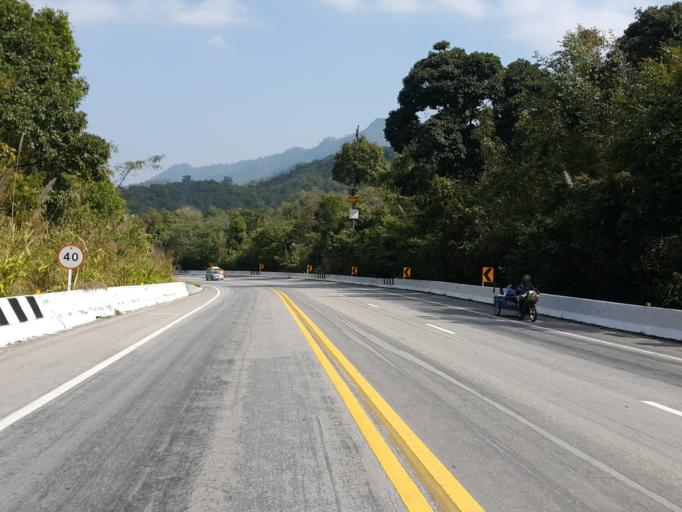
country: TH
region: Lampang
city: Wang Nuea
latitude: 19.0687
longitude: 99.3848
